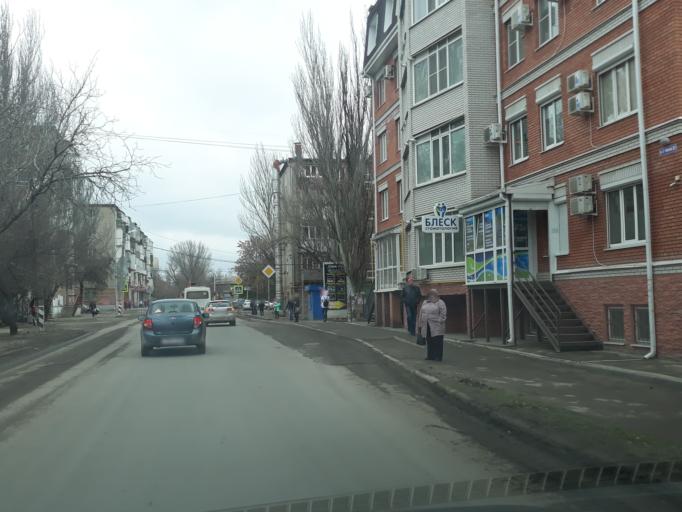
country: RU
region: Rostov
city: Taganrog
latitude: 47.2665
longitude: 38.9211
